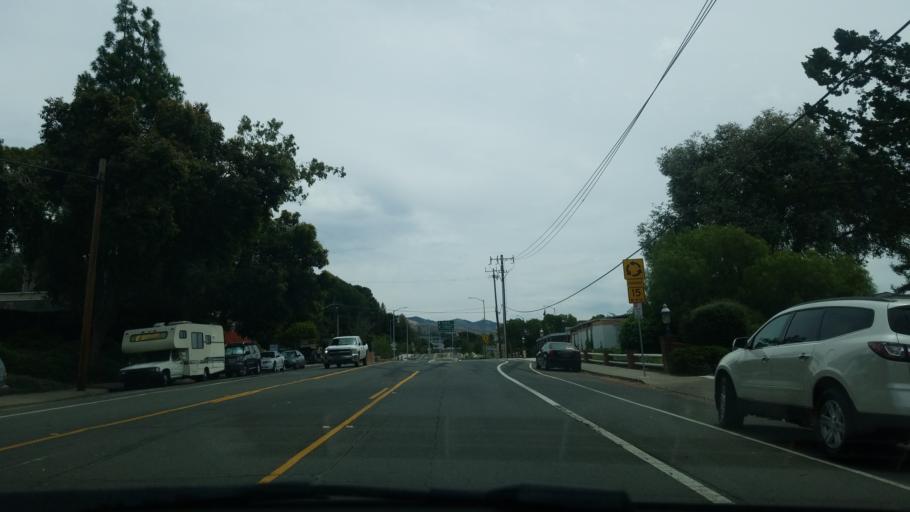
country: US
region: California
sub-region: San Luis Obispo County
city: San Luis Obispo
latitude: 35.2614
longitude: -120.6413
